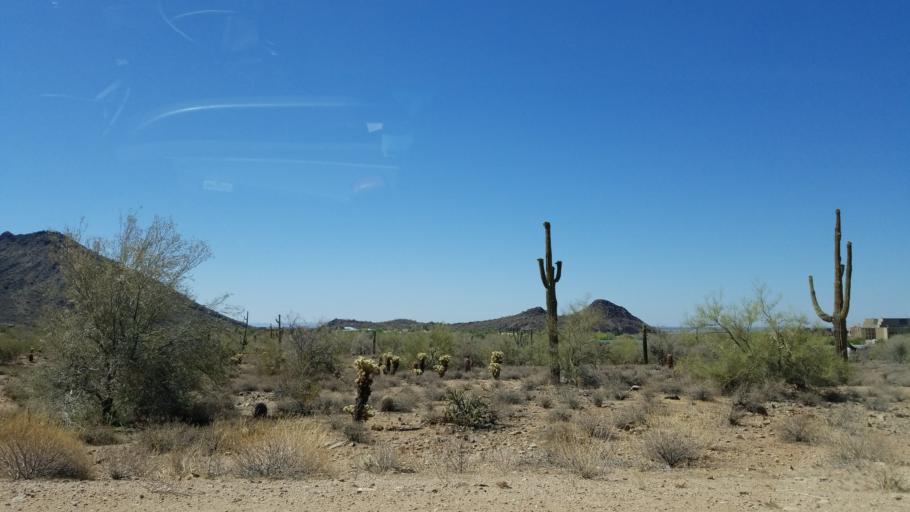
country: US
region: Arizona
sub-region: Maricopa County
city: Fountain Hills
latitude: 33.5896
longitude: -111.7915
